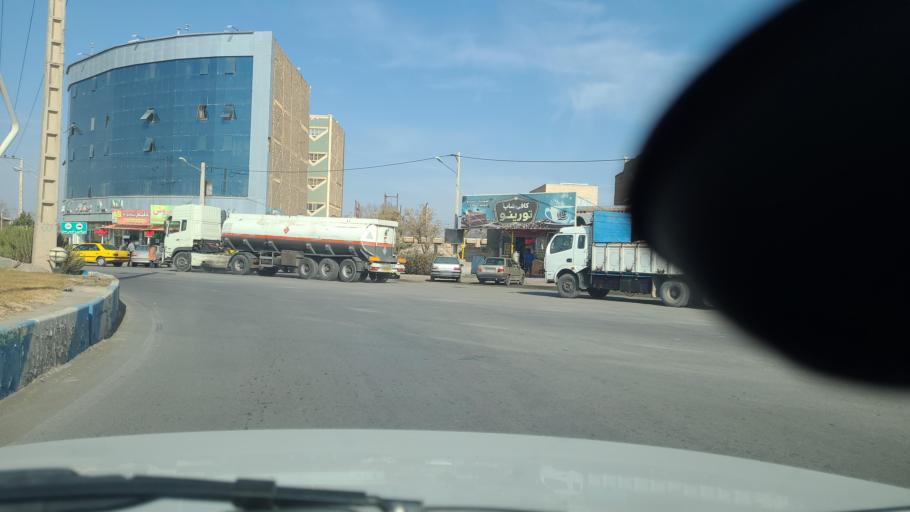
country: IR
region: Razavi Khorasan
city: Fariman
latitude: 35.6945
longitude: 59.8447
